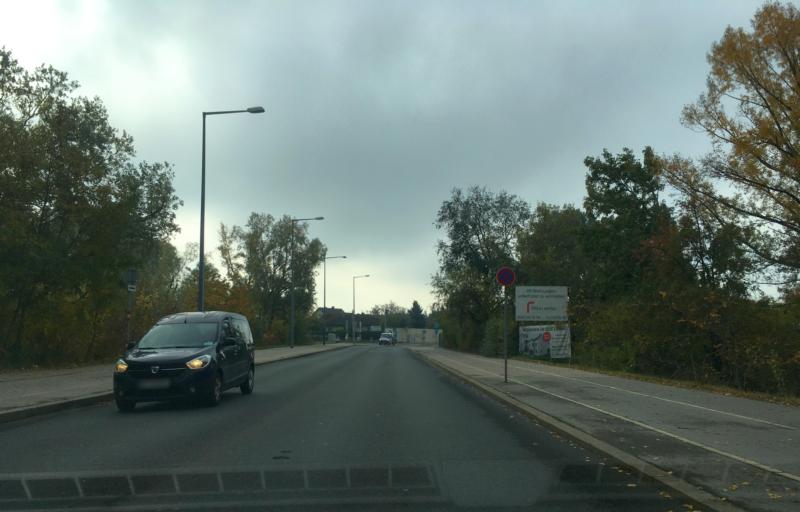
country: AT
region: Lower Austria
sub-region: Politischer Bezirk Wien-Umgebung
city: Schwechat
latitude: 48.2055
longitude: 16.4762
